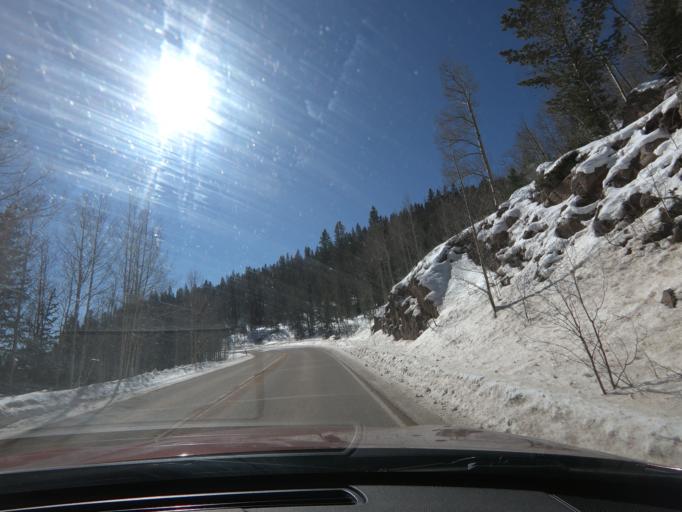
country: US
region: Colorado
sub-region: Teller County
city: Cripple Creek
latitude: 38.7499
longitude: -105.1021
